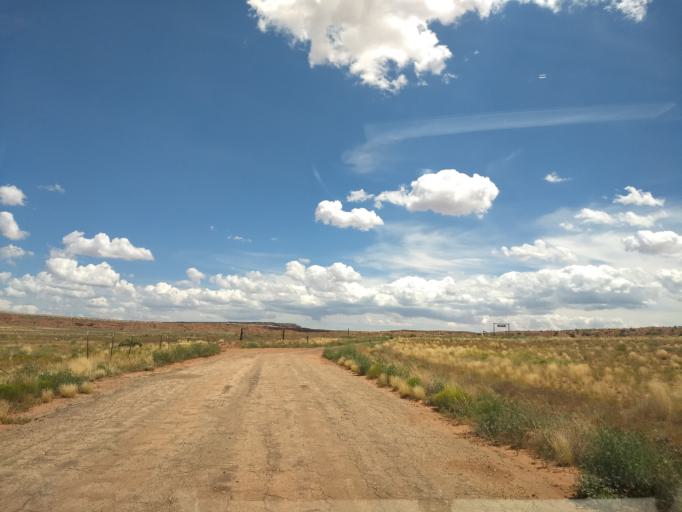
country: US
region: Arizona
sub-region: Coconino County
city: Fredonia
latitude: 36.9455
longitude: -112.5025
